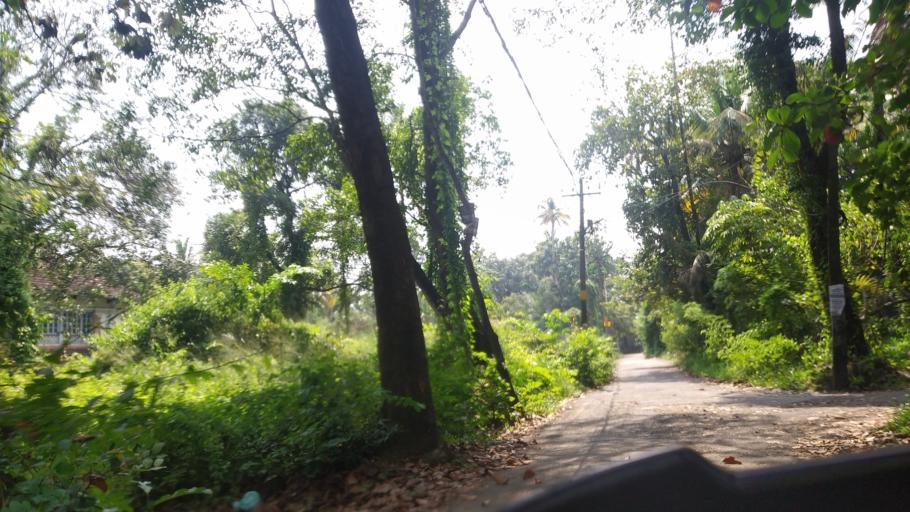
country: IN
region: Kerala
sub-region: Ernakulam
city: Elur
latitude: 10.0542
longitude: 76.2185
